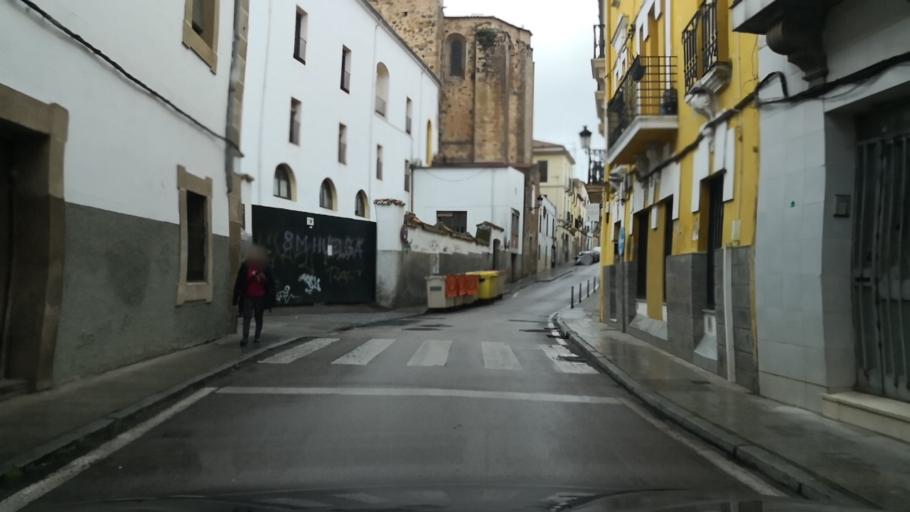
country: ES
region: Extremadura
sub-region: Provincia de Caceres
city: Caceres
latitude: 39.4764
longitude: -6.3713
